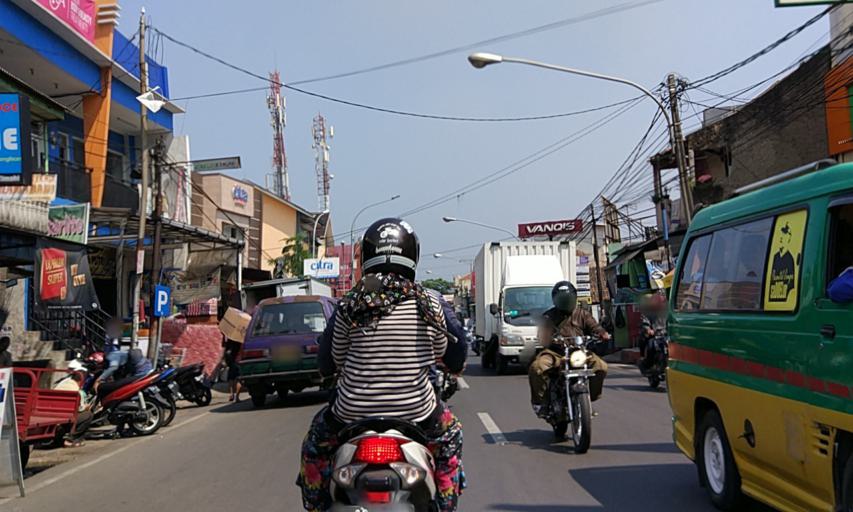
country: ID
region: West Java
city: Cimahi
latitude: -6.8969
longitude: 107.5593
